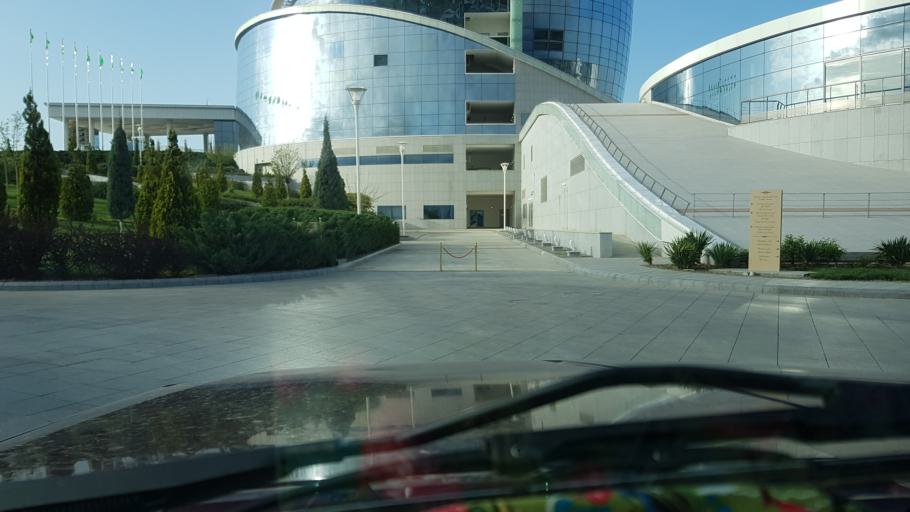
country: TM
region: Ahal
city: Ashgabat
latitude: 37.9283
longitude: 58.3332
